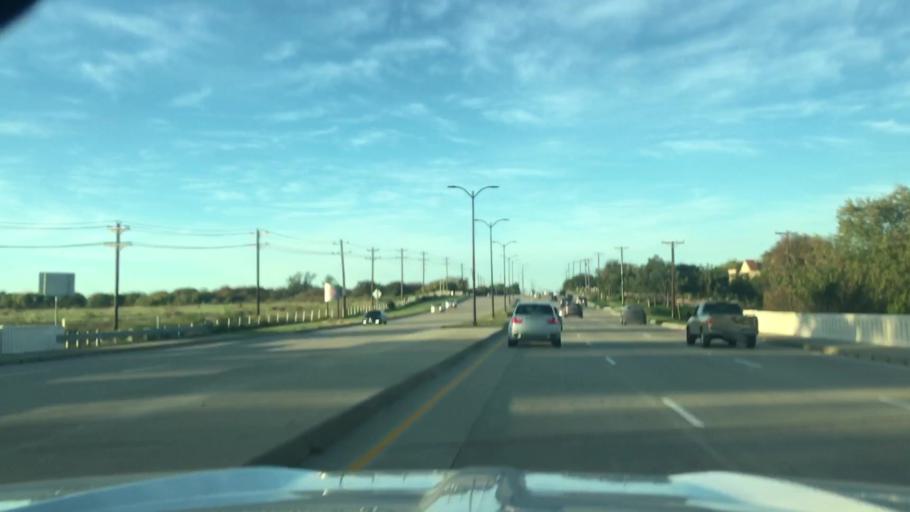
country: US
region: Texas
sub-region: Collin County
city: Frisco
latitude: 33.1787
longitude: -96.8029
